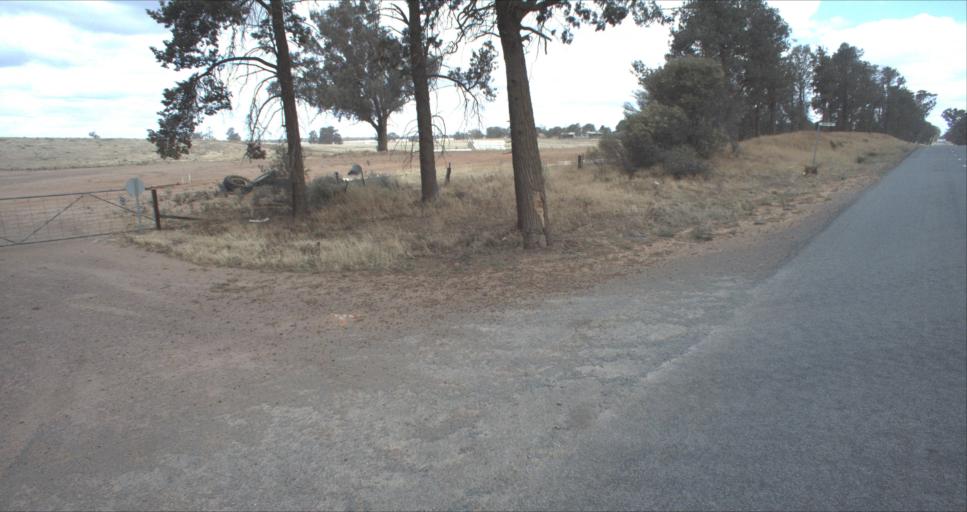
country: AU
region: New South Wales
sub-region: Leeton
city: Leeton
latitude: -34.6580
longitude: 146.3499
